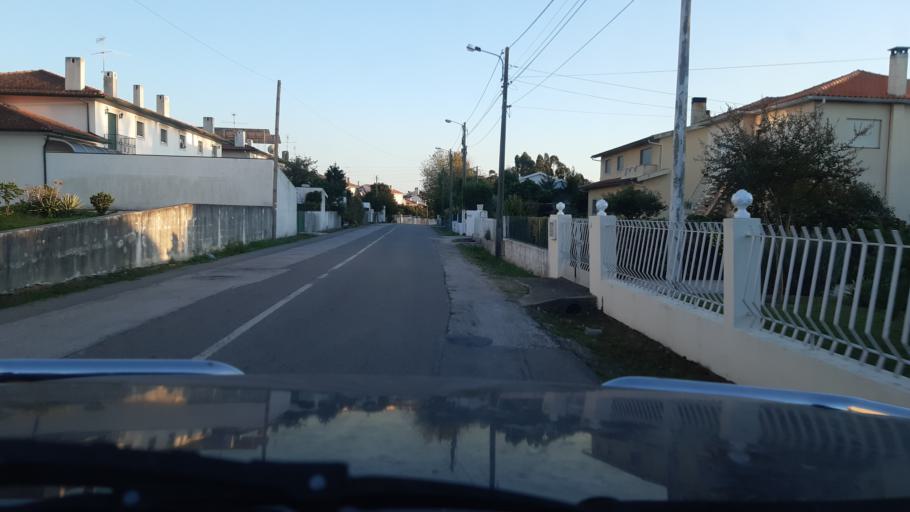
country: PT
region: Aveiro
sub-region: Agueda
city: Agueda
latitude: 40.5810
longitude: -8.4638
